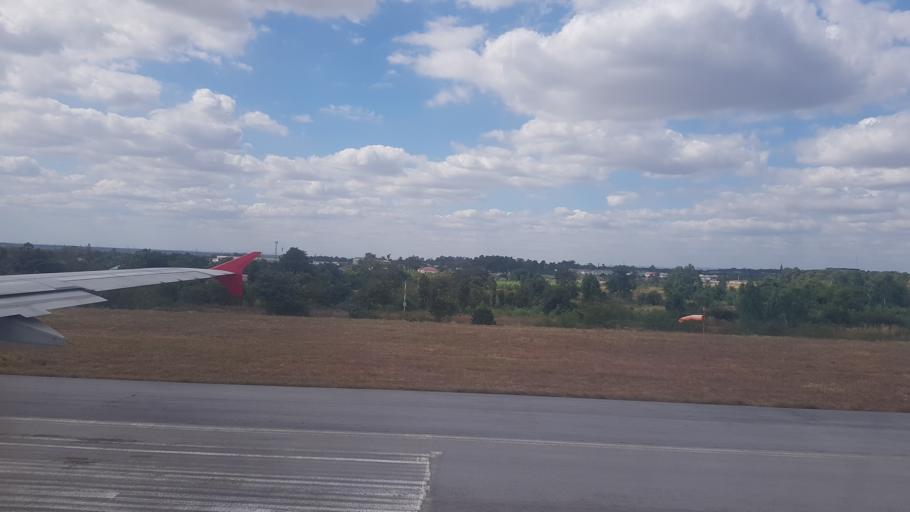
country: TH
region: Khon Kaen
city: Khon Kaen
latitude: 16.4597
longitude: 102.7791
